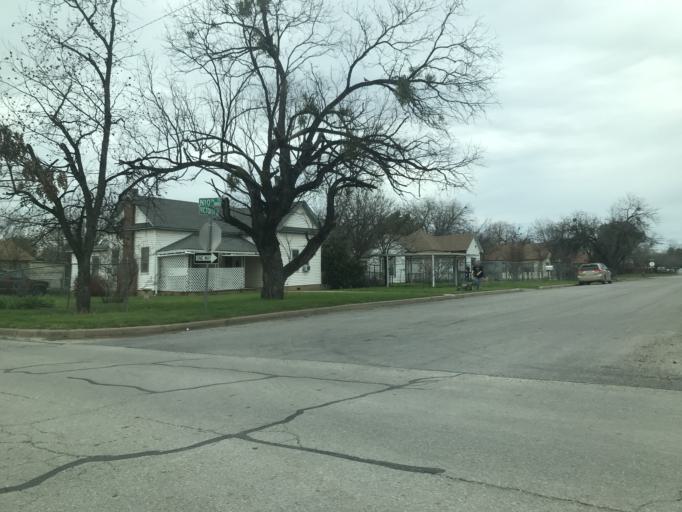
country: US
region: Texas
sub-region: Taylor County
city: Abilene
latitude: 32.4605
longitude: -99.7454
